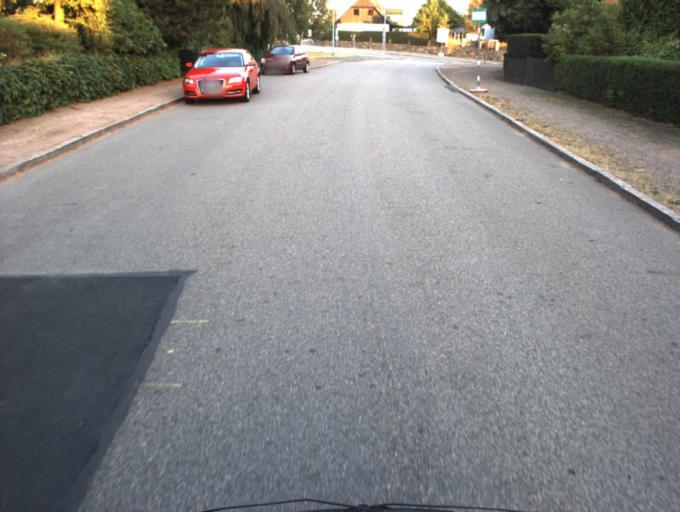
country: SE
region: Skane
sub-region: Helsingborg
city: Helsingborg
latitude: 56.0317
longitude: 12.7313
